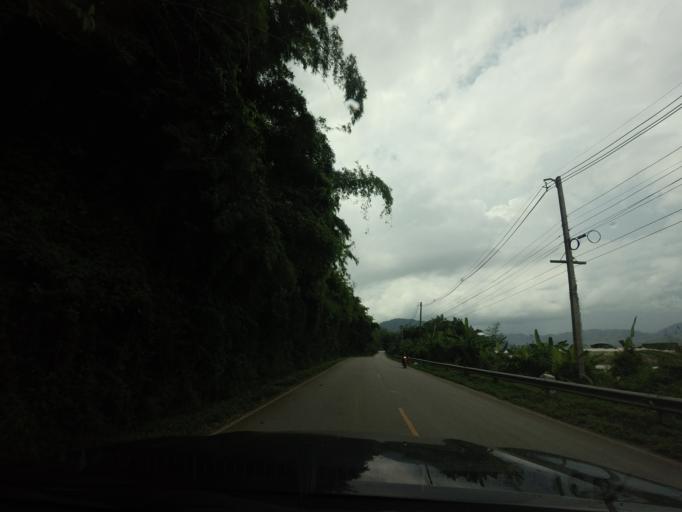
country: TH
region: Loei
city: Pak Chom
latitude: 18.0534
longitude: 101.8163
